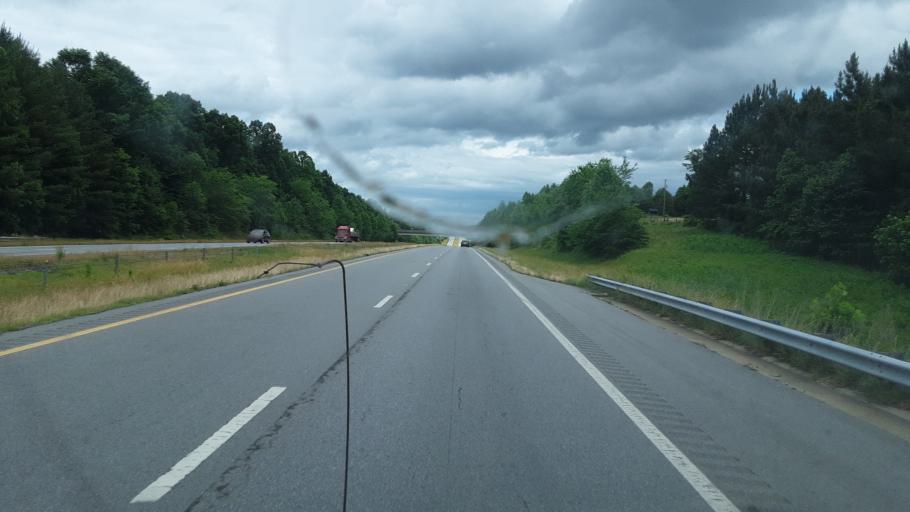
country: US
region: North Carolina
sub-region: Yadkin County
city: Yadkinville
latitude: 36.1178
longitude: -80.7327
